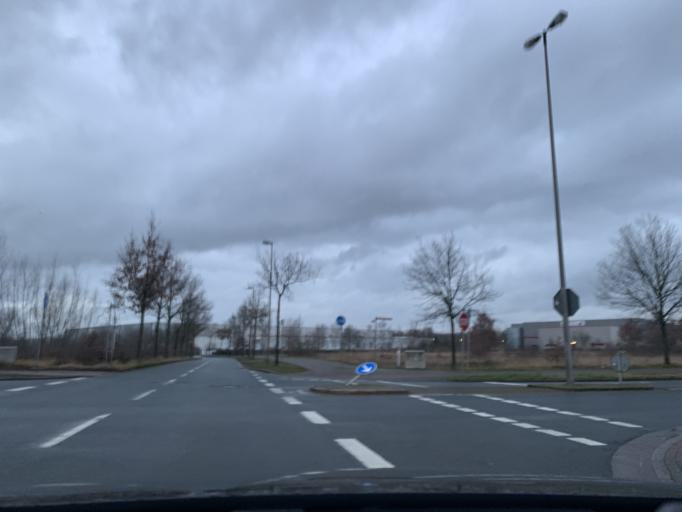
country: DE
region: Lower Saxony
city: Ritterhude
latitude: 53.1399
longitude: 8.7025
